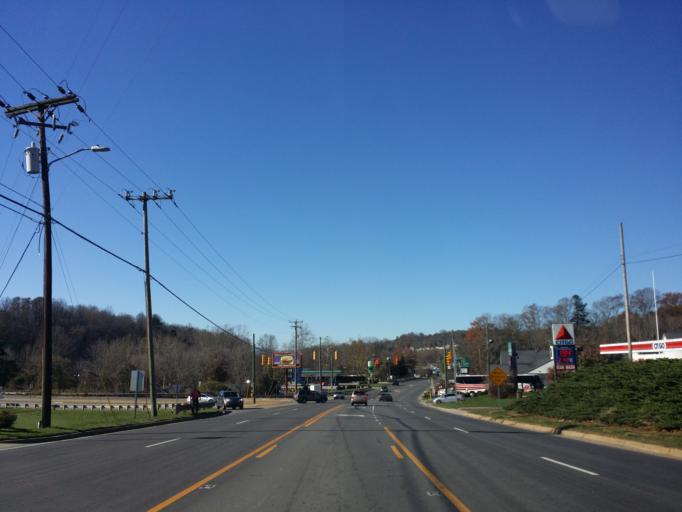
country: US
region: North Carolina
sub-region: Buncombe County
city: Swannanoa
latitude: 35.5843
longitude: -82.4622
